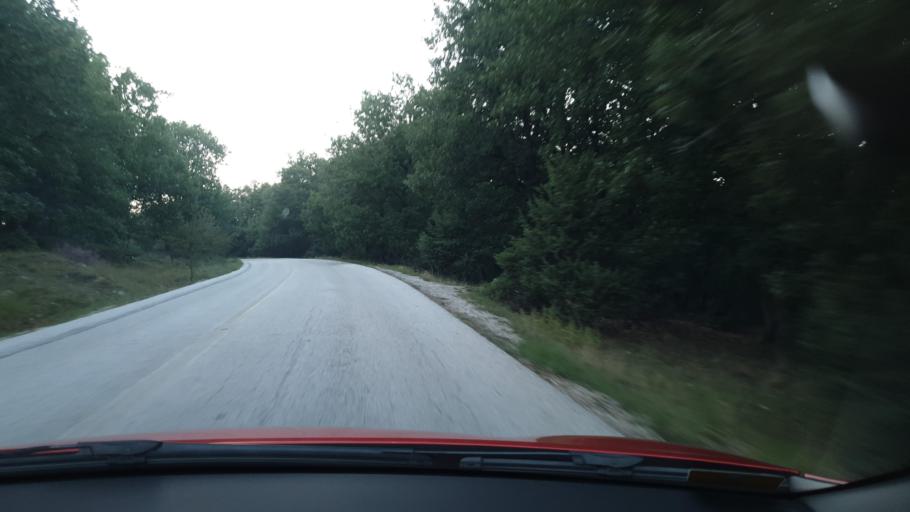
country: GR
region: Central Macedonia
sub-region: Nomos Thessalonikis
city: Peristera
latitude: 40.5155
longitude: 23.2141
